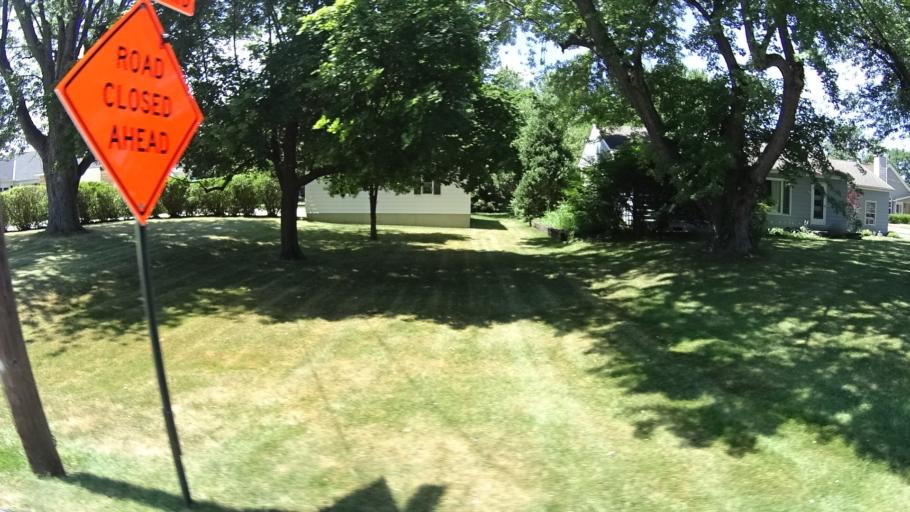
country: US
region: Ohio
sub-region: Erie County
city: Sandusky
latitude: 41.3969
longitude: -82.6753
